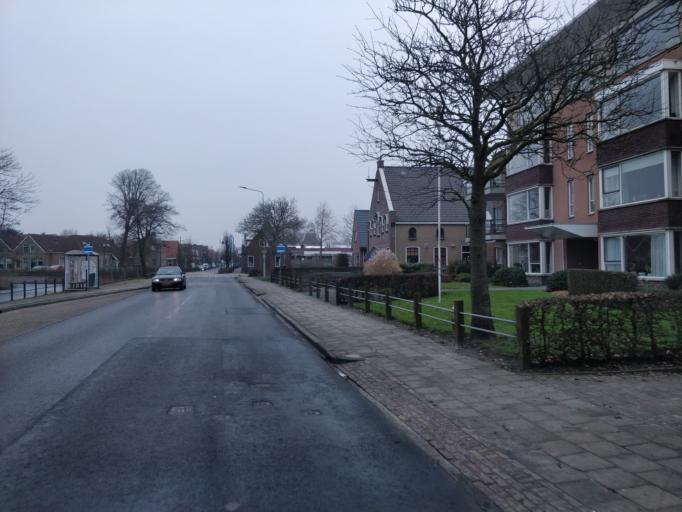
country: NL
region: Friesland
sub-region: Gemeente Het Bildt
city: Sint Annaparochie
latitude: 53.2738
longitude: 5.6578
